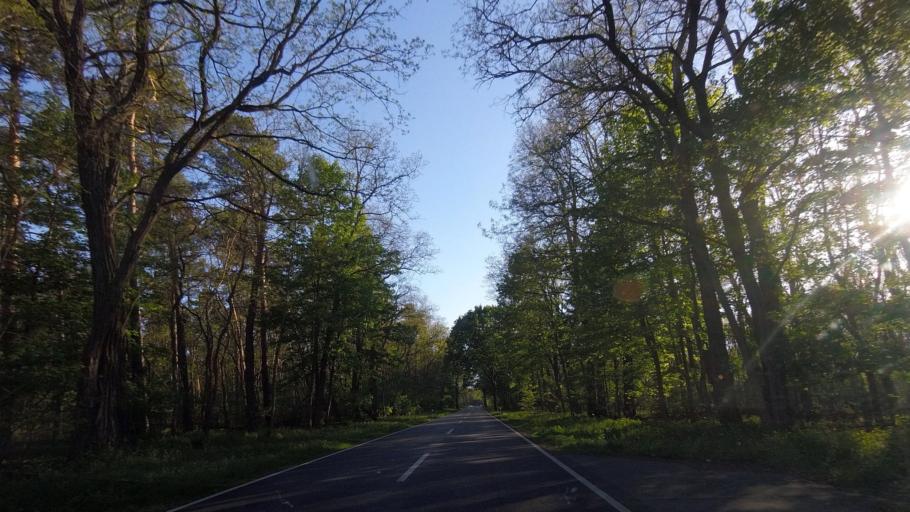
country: DE
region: Brandenburg
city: Baruth
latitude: 52.0228
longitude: 13.4649
